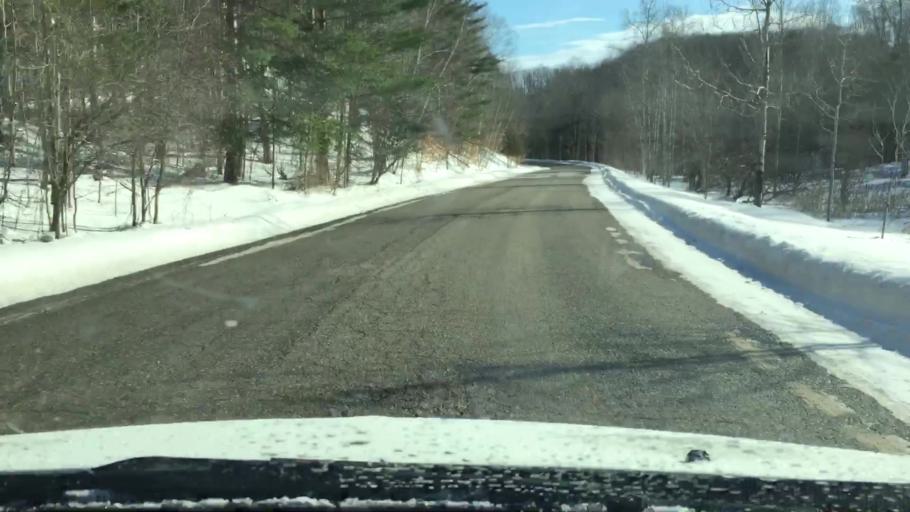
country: US
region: Michigan
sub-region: Charlevoix County
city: East Jordan
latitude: 45.1049
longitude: -85.1462
